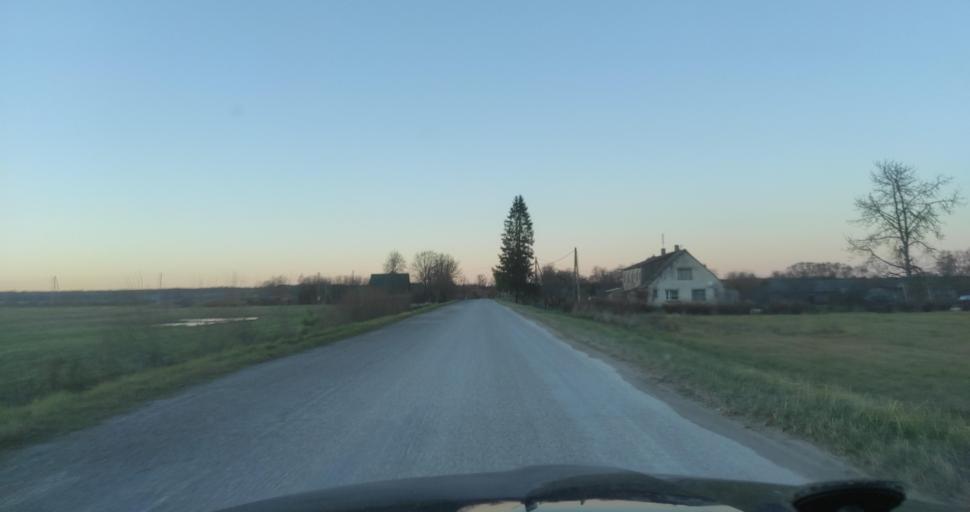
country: LV
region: Dundaga
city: Dundaga
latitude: 57.3719
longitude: 22.2328
